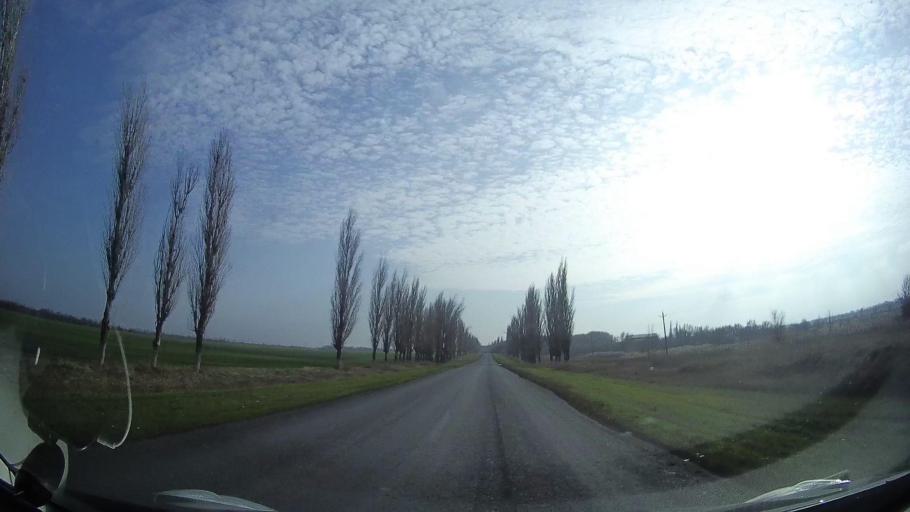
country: RU
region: Rostov
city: Mechetinskaya
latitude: 46.8310
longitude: 40.5509
